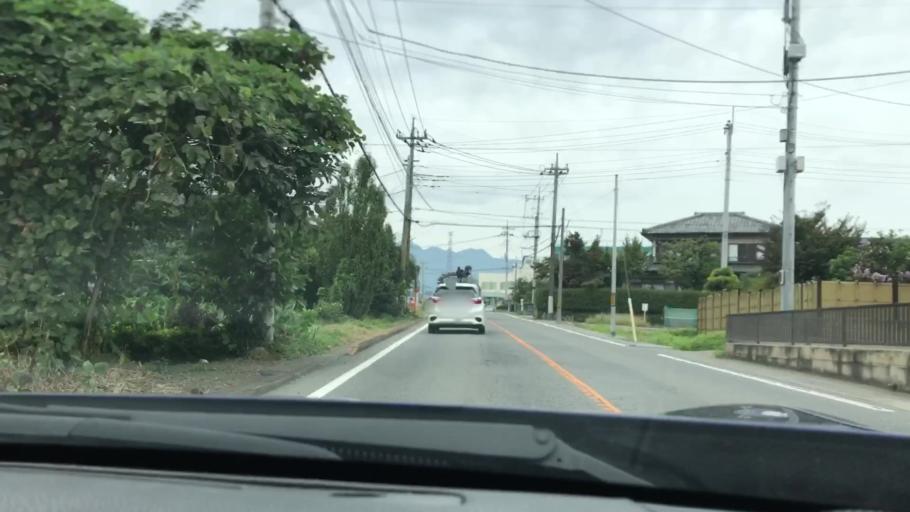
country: JP
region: Gunma
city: Kanekomachi
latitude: 36.3984
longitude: 138.9918
